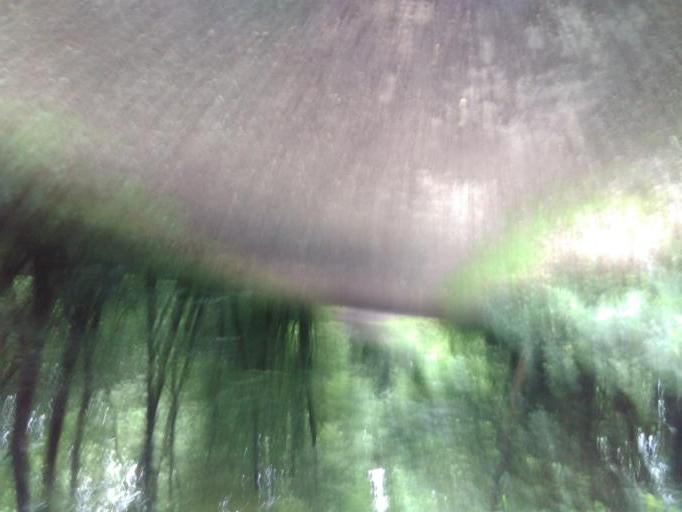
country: FR
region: Pays de la Loire
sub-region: Departement de la Vendee
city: La Ferriere
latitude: 46.7029
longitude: -1.3211
